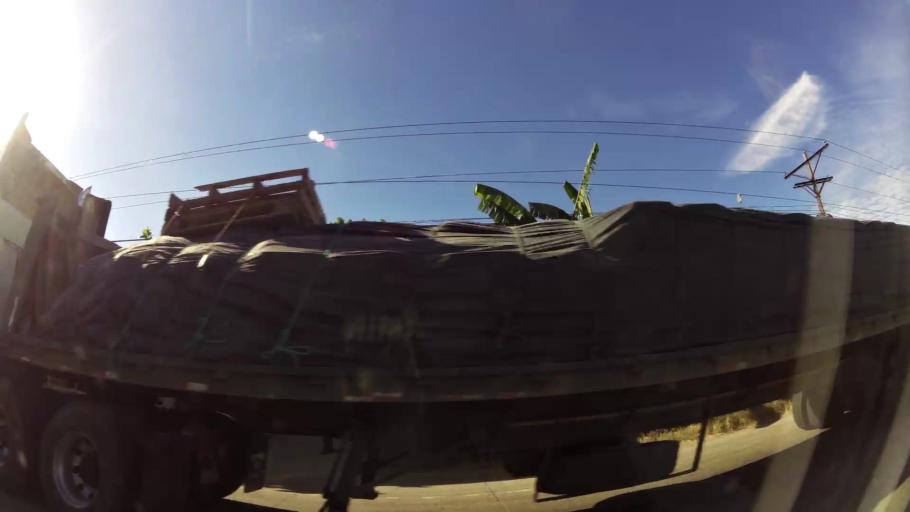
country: SV
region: Santa Ana
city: Santa Ana
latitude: 14.0277
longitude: -89.5290
